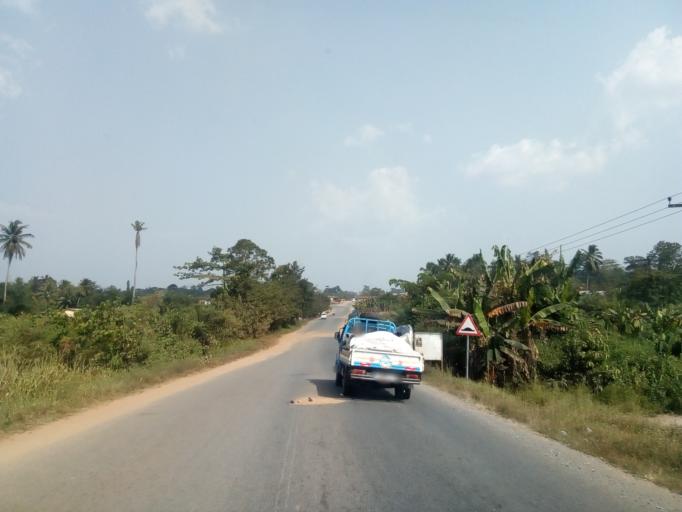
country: GH
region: Eastern
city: Suhum
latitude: 6.0450
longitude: -0.4163
